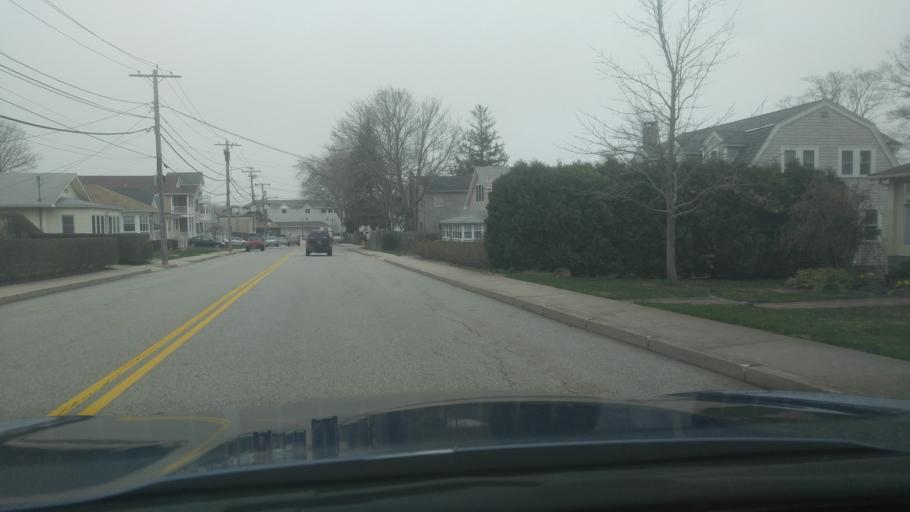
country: US
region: Rhode Island
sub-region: Washington County
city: Narragansett Pier
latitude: 41.4294
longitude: -71.4586
